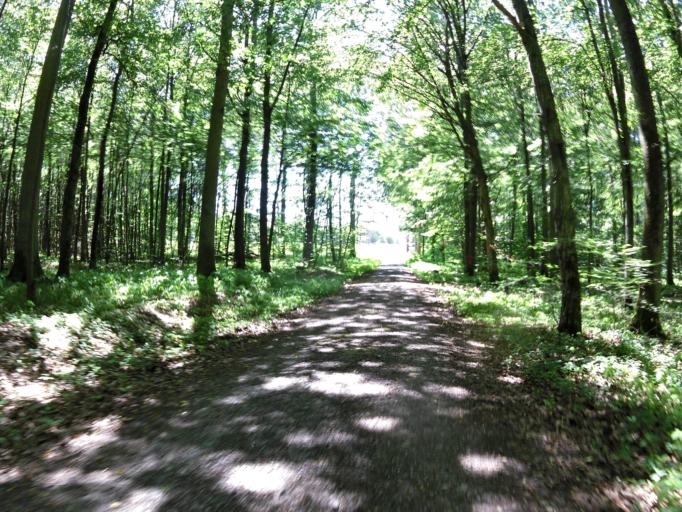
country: DE
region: Bavaria
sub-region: Regierungsbezirk Unterfranken
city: Kleinrinderfeld
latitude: 49.7052
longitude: 9.8647
